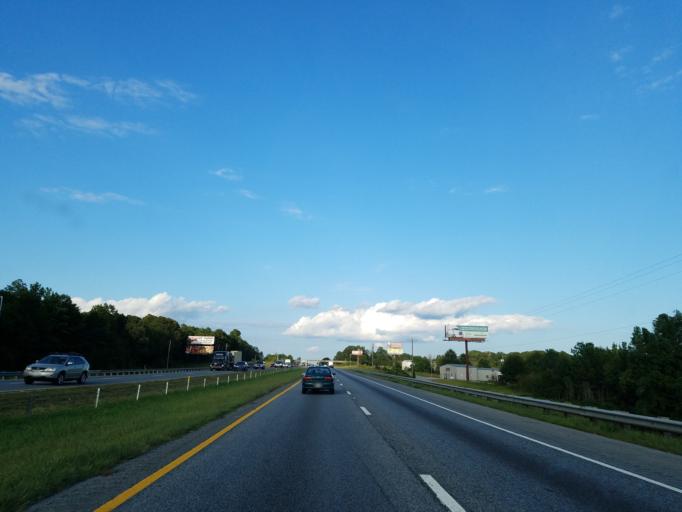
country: US
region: South Carolina
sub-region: Spartanburg County
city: Cowpens
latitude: 35.0533
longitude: -81.7938
